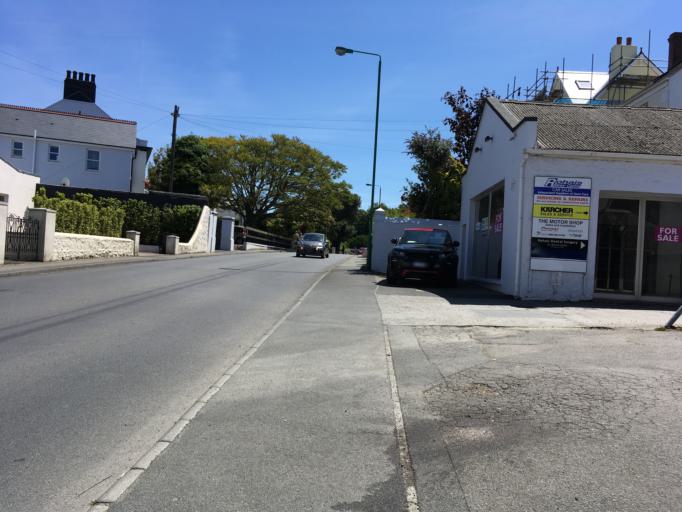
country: GG
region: St Peter Port
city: Saint Peter Port
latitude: 49.4595
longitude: -2.5553
